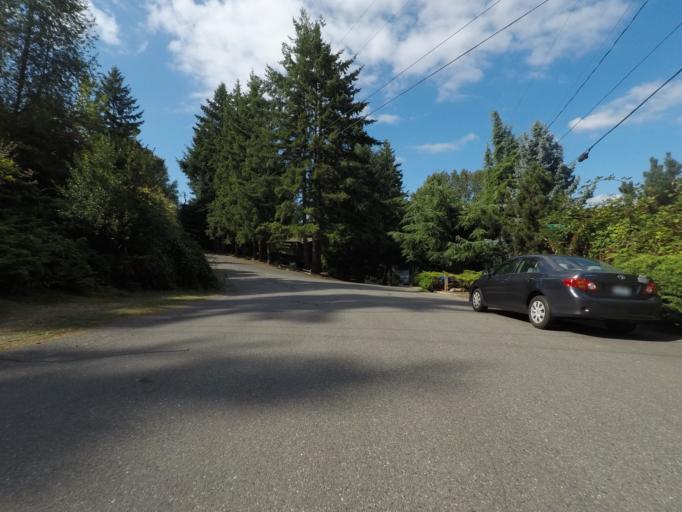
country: US
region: Washington
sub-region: Snohomish County
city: Brier
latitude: 47.7758
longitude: -122.2578
